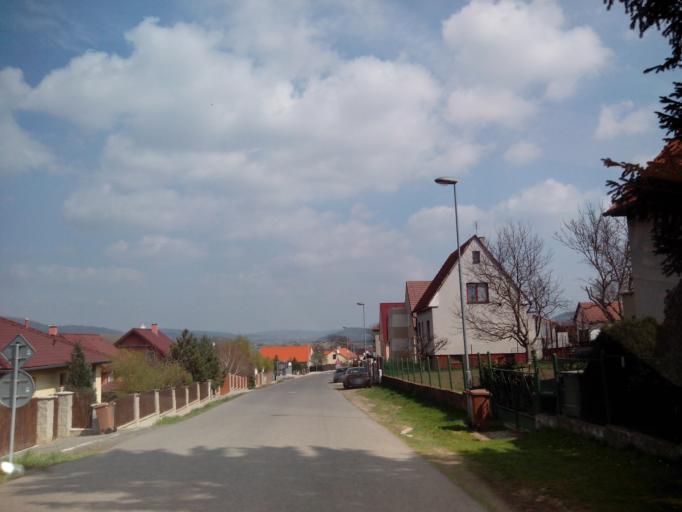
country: CZ
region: Central Bohemia
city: Zdice
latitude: 49.8825
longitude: 13.9556
